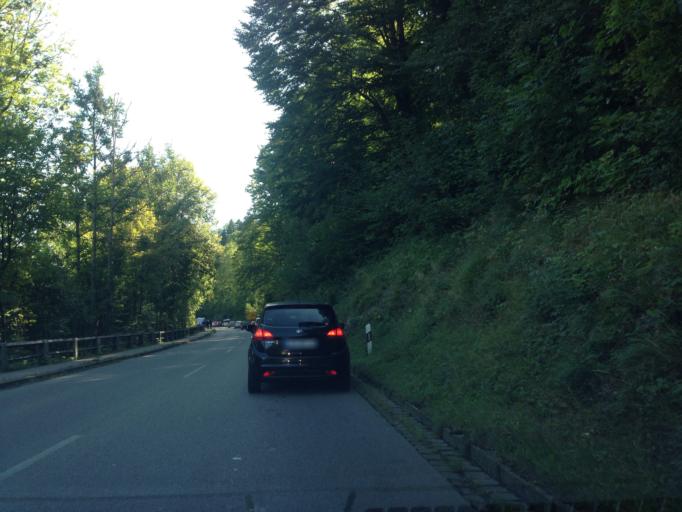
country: DE
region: Bavaria
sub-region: Swabia
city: Fuessen
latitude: 47.5649
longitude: 10.7056
